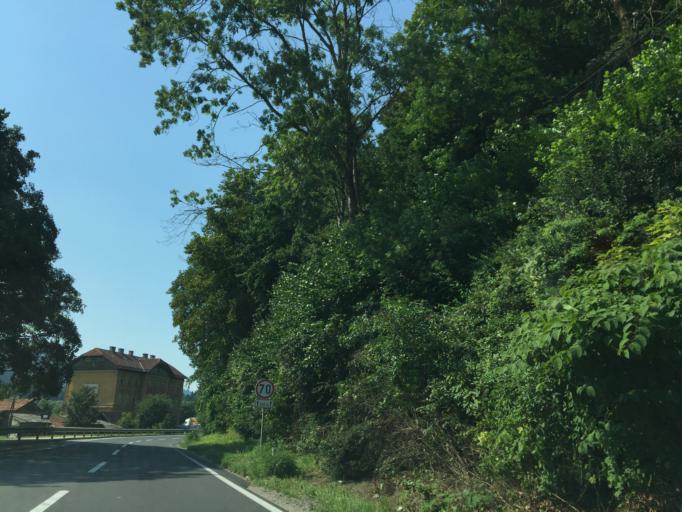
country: SI
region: Dravograd
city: Dravograd
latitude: 46.5724
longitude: 15.0328
